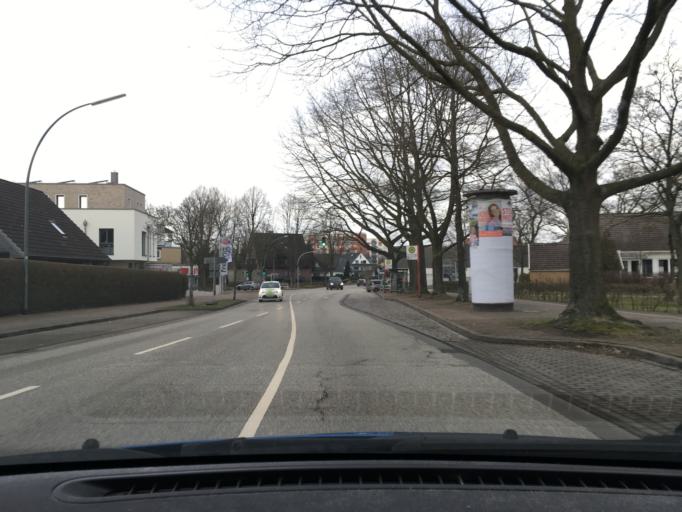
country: DE
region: Schleswig-Holstein
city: Wedel
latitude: 53.5753
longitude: 9.7127
